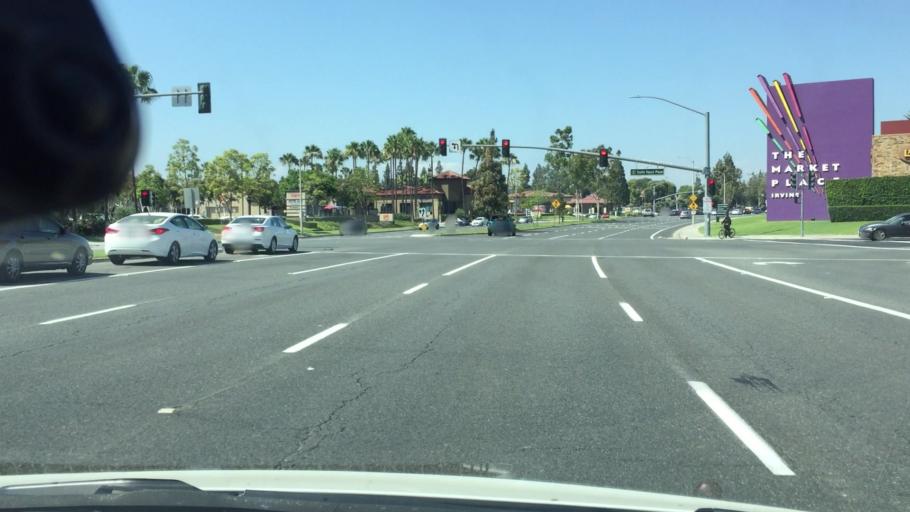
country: US
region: California
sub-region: Orange County
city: North Tustin
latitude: 33.7280
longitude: -117.7887
